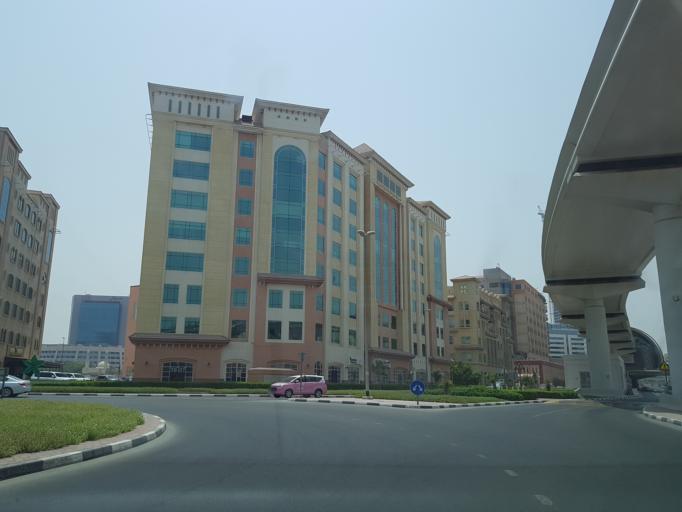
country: AE
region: Ash Shariqah
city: Sharjah
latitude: 25.2307
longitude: 55.3257
